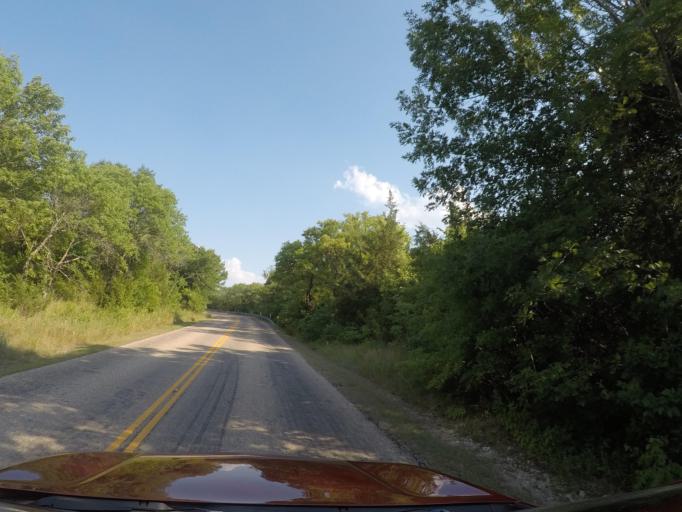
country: US
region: Texas
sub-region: Grayson County
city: Preston
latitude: 33.8118
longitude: -96.6089
